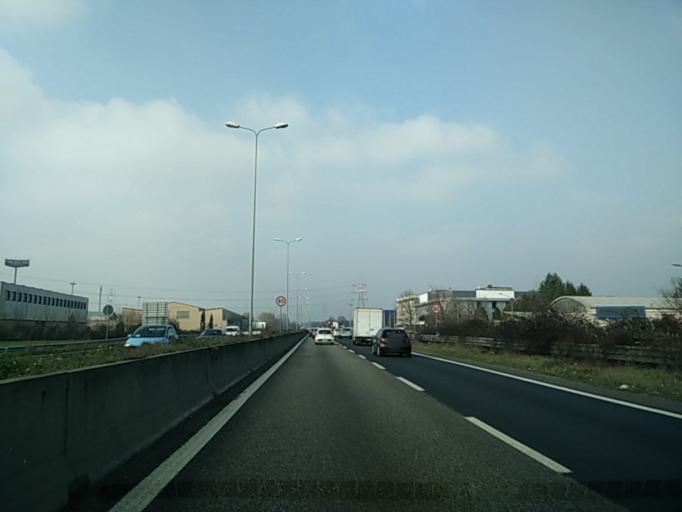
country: IT
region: Lombardy
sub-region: Provincia di Monza e Brianza
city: Varedo
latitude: 45.5895
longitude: 9.1737
